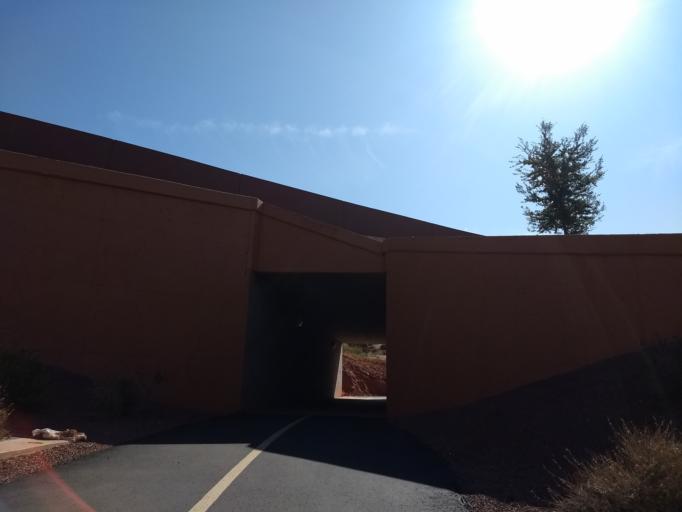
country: US
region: Utah
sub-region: Washington County
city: Saint George
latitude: 37.1331
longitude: -113.6028
